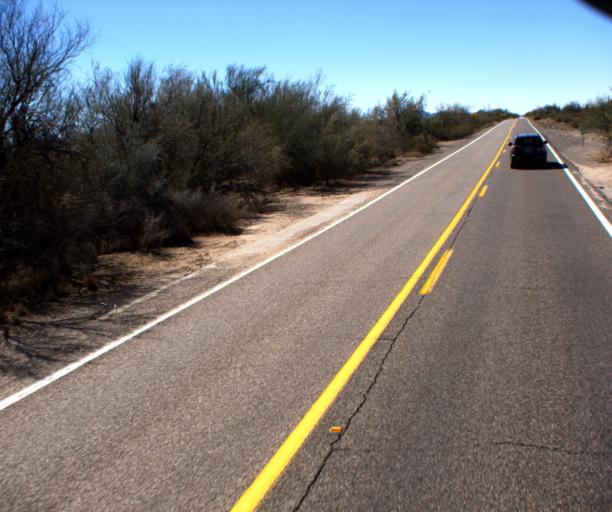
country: US
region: Arizona
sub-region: Pima County
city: Ajo
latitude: 32.1832
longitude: -112.7614
